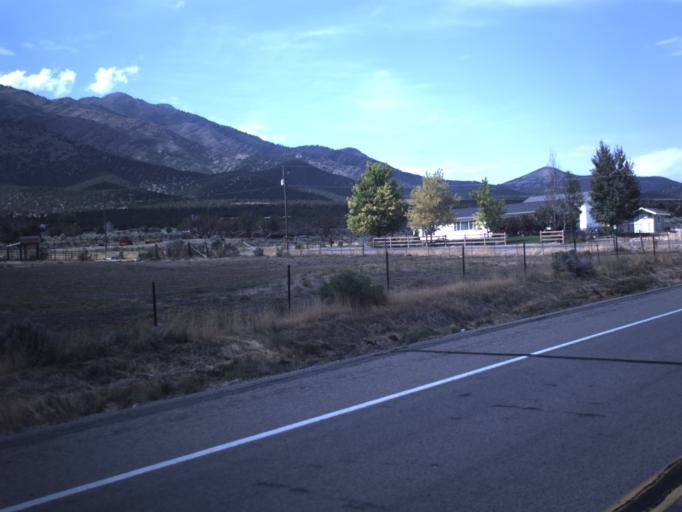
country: US
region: Utah
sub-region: Utah County
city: Eagle Mountain
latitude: 40.3299
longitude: -112.1023
